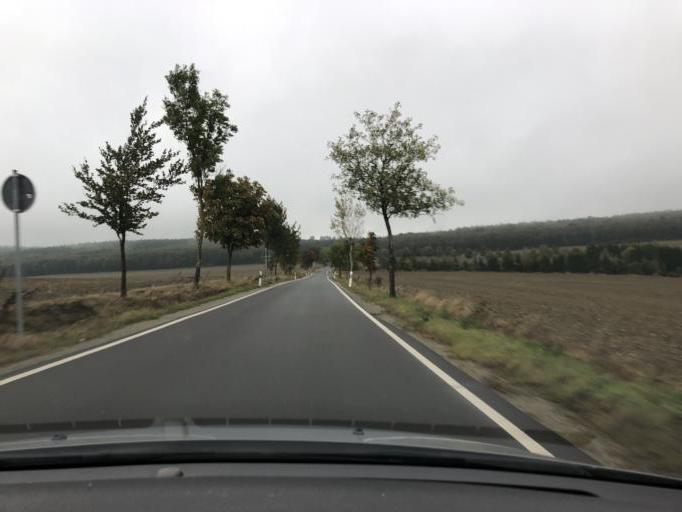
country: DE
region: Thuringia
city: Kreuzebra
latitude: 51.3522
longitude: 10.2614
